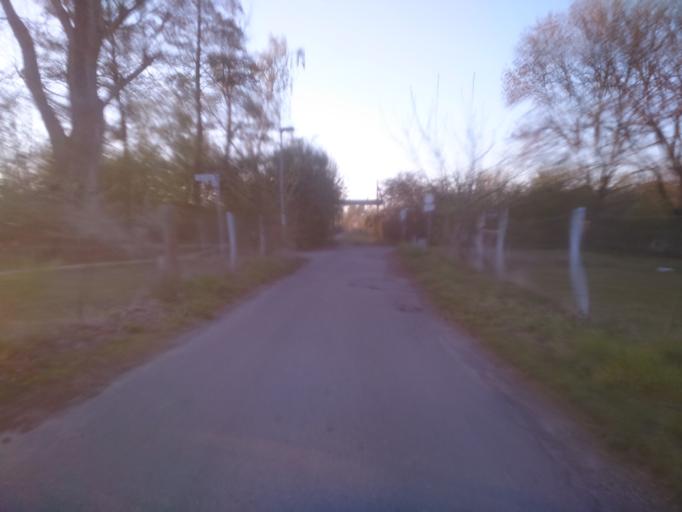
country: DE
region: Berlin
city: Stadtrandsiedlung Malchow
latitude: 52.5742
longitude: 13.4702
